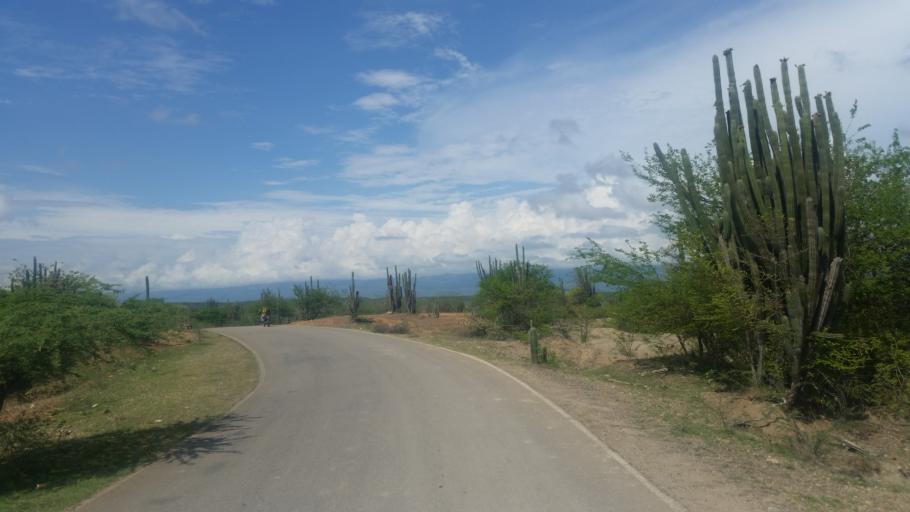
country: CO
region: Huila
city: Villavieja
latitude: 3.2321
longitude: -75.1766
